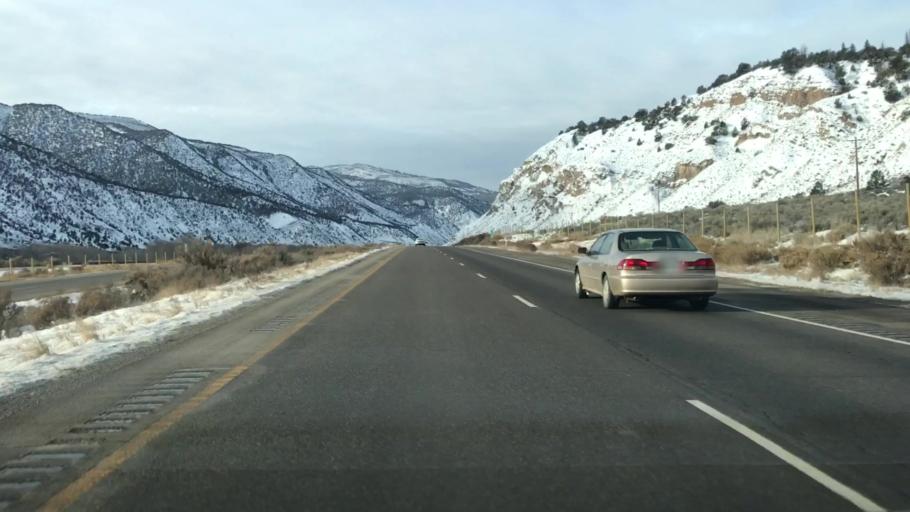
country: US
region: Colorado
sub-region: Eagle County
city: Gypsum
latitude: 39.6550
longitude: -106.9814
